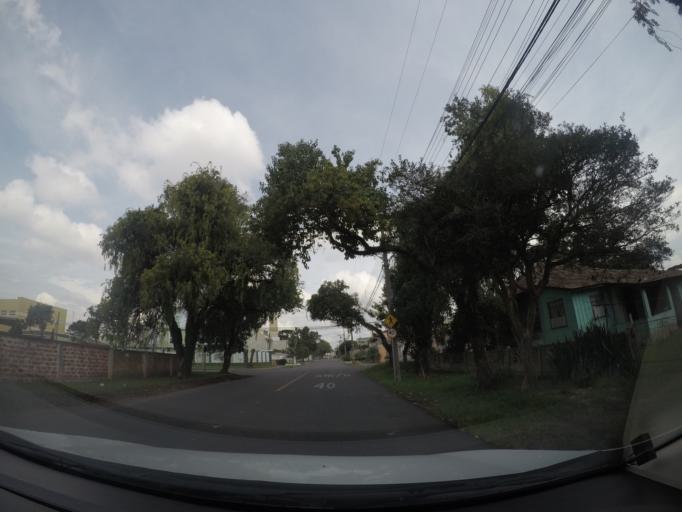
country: BR
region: Parana
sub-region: Curitiba
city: Curitiba
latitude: -25.4763
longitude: -49.2617
